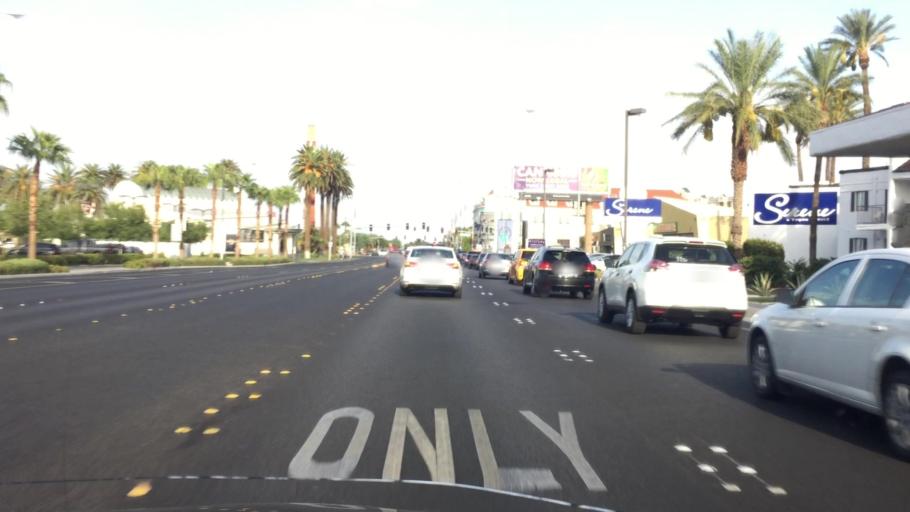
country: US
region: Nevada
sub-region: Clark County
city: Paradise
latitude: 36.1080
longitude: -115.1543
